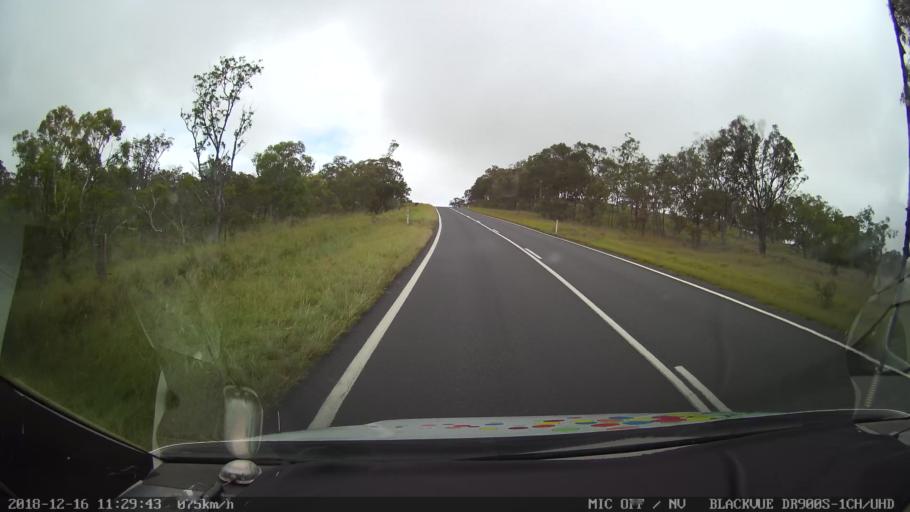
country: AU
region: New South Wales
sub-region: Tenterfield Municipality
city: Carrolls Creek
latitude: -29.0364
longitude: 152.1127
